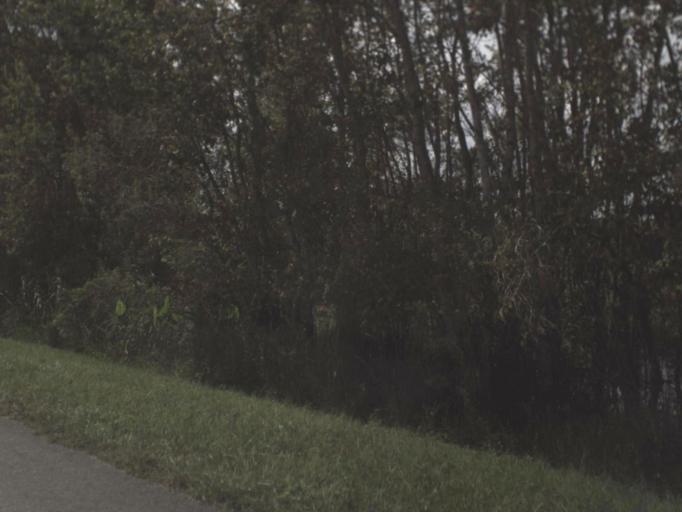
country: US
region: Florida
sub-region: Collier County
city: Immokalee
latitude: 26.2083
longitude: -81.3460
